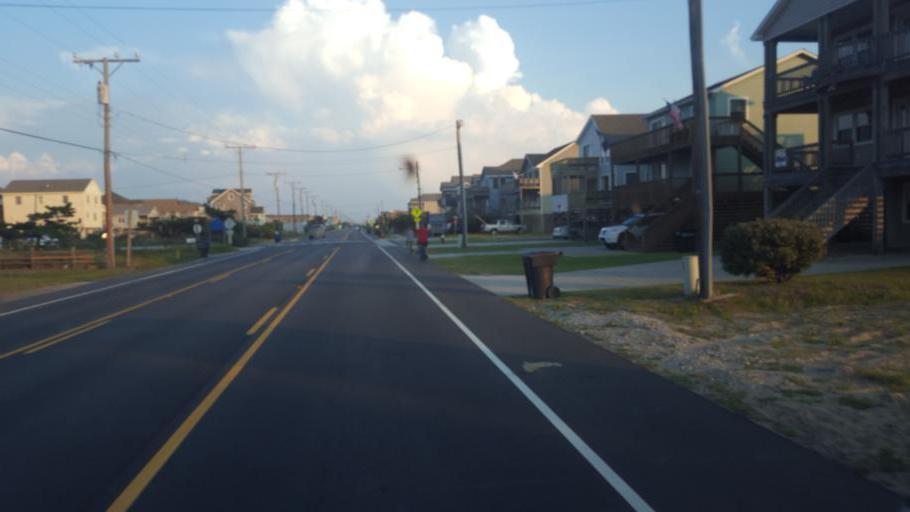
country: US
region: North Carolina
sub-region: Dare County
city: Nags Head
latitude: 35.9948
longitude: -75.6458
